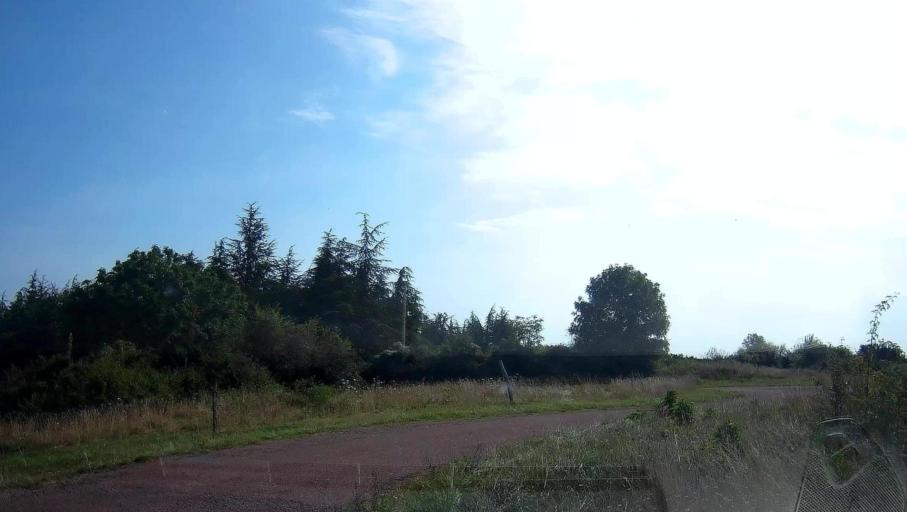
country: FR
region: Bourgogne
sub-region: Departement de la Cote-d'Or
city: Nolay
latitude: 46.9031
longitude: 4.6114
